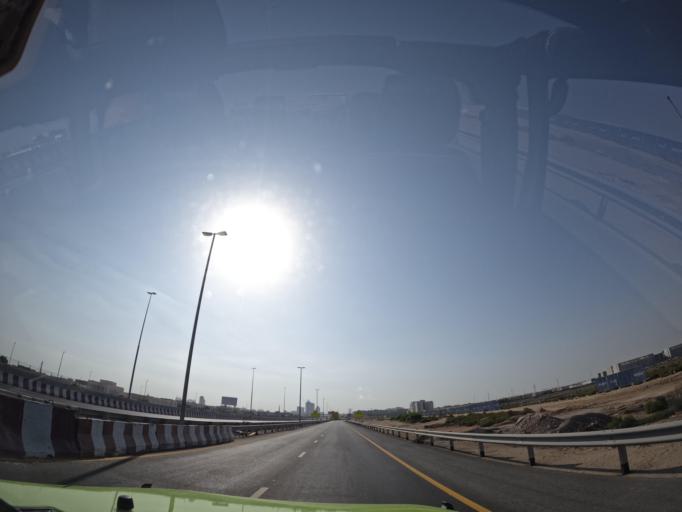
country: AE
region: Dubai
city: Dubai
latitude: 25.1342
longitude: 55.3517
